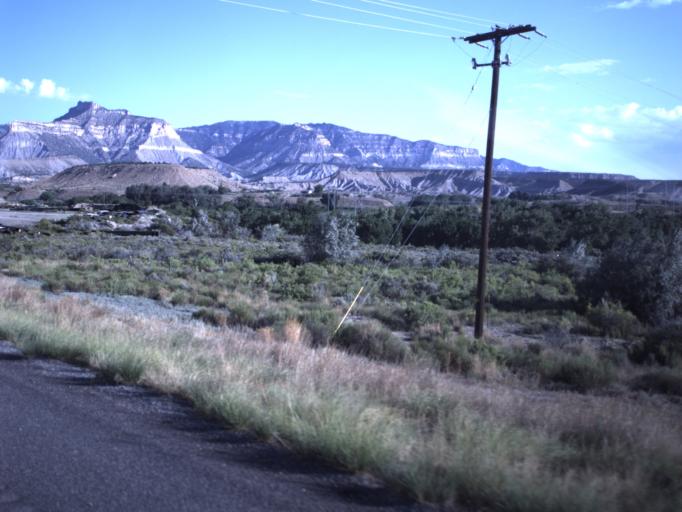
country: US
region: Utah
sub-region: Emery County
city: Huntington
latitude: 39.3431
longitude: -110.9842
